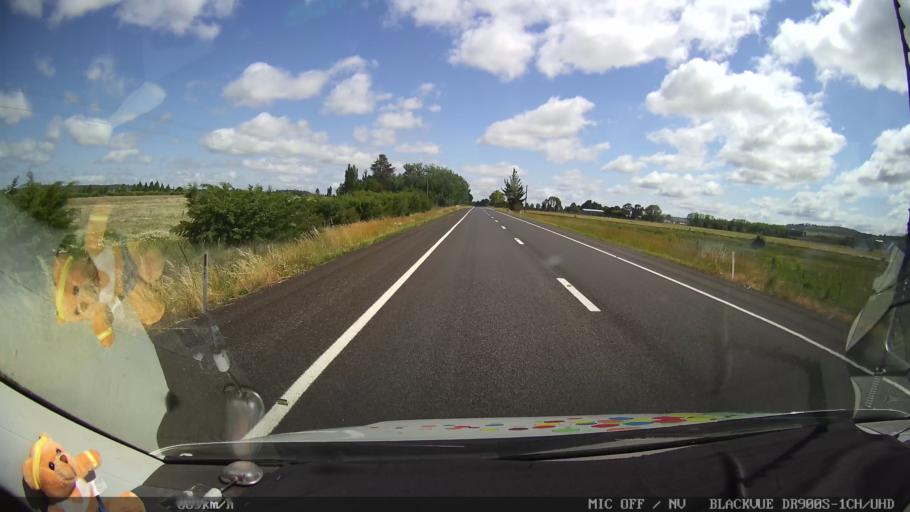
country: AU
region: New South Wales
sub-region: Glen Innes Severn
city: Glen Innes
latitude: -29.8238
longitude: 151.7394
